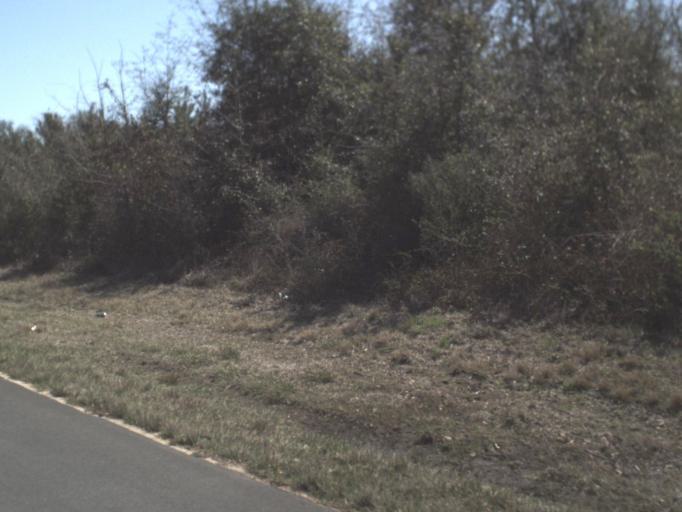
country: US
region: Florida
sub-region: Jackson County
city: Malone
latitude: 30.8698
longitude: -85.1345
